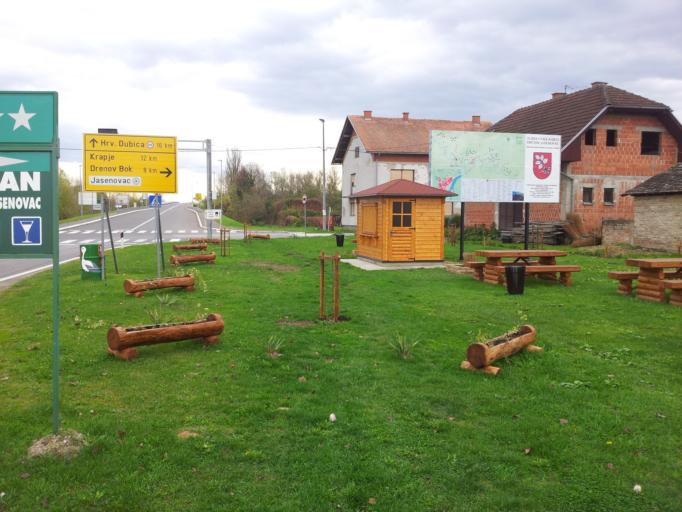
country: HR
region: Sisacko-Moslavacka
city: Novska
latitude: 45.2709
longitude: 16.9109
